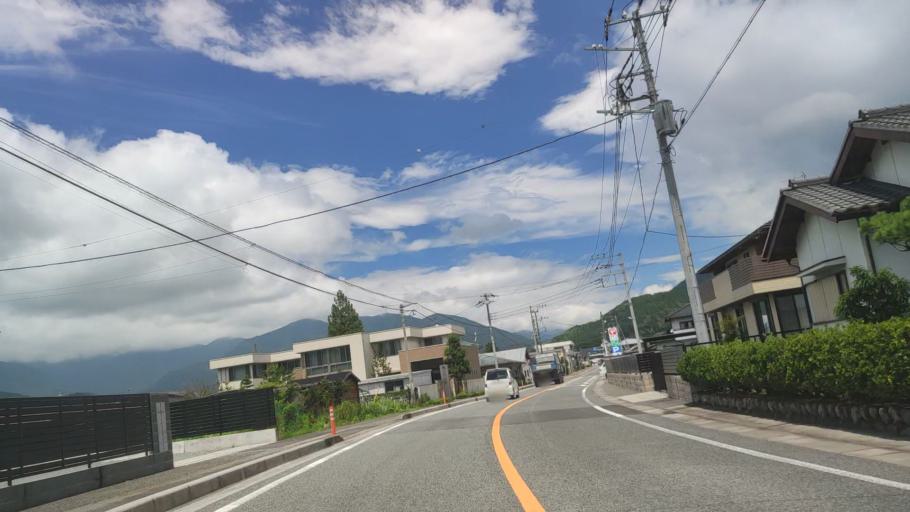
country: JP
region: Shizuoka
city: Fujinomiya
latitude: 35.2757
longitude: 138.4681
